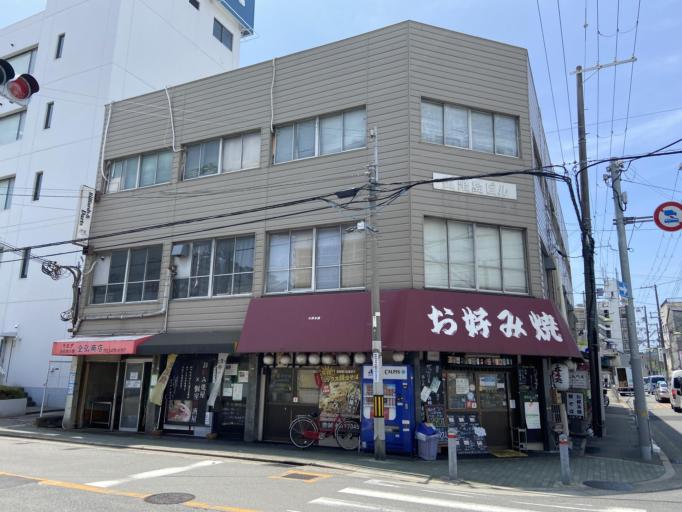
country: JP
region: Hyogo
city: Amagasaki
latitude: 34.7145
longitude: 135.4547
